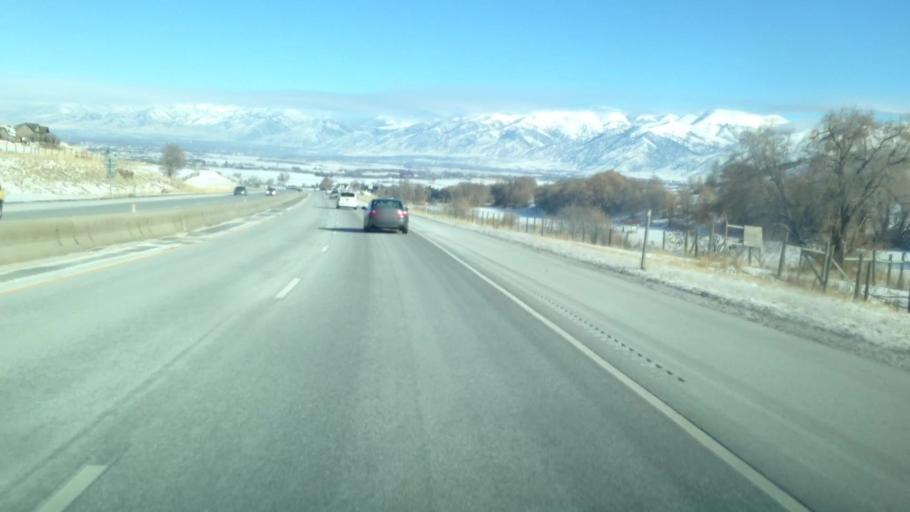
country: US
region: Utah
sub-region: Cache County
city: Wellsville
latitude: 41.6026
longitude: -111.9458
